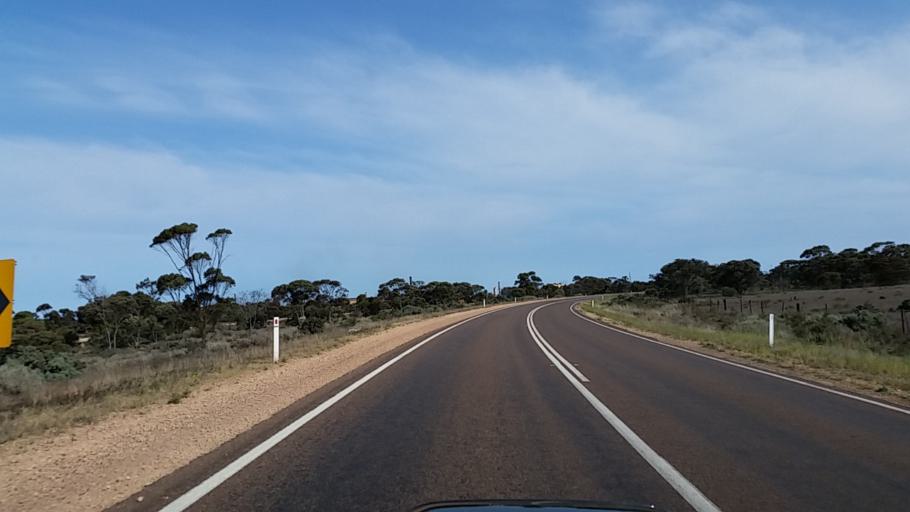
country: AU
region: South Australia
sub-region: Whyalla
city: Whyalla
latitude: -32.9835
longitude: 137.5821
